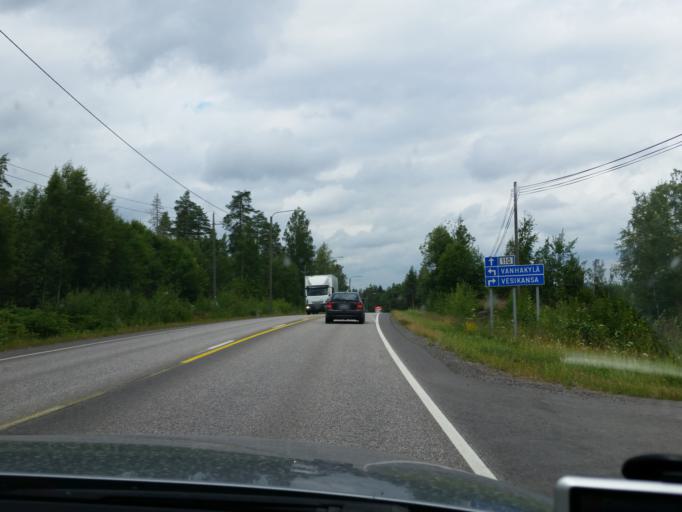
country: FI
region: Uusimaa
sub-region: Helsinki
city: Vihti
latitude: 60.3402
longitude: 24.1965
